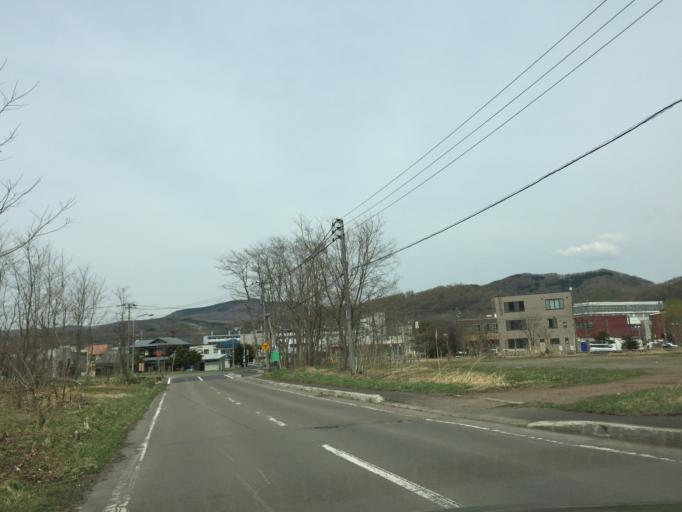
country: JP
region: Hokkaido
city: Akabira
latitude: 43.5507
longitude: 142.0549
